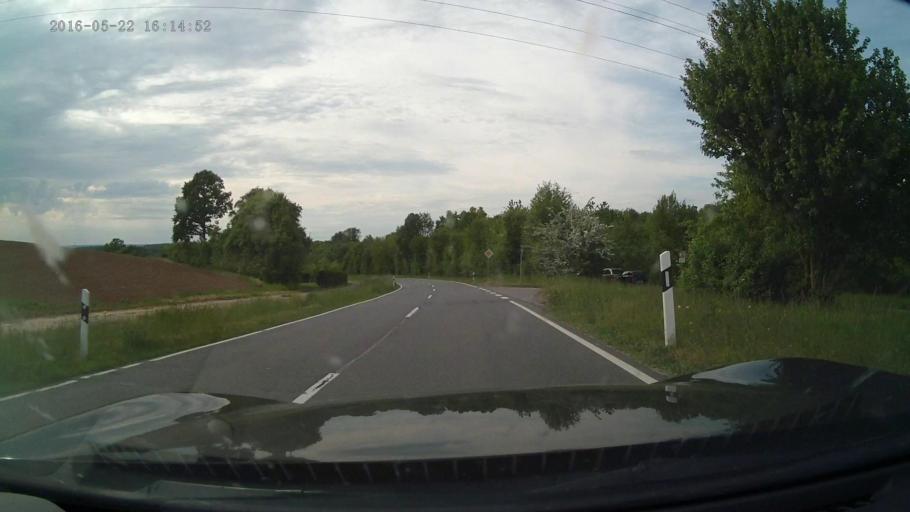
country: DE
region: Baden-Wuerttemberg
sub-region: Karlsruhe Region
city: Osterburken
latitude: 49.4249
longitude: 9.4396
